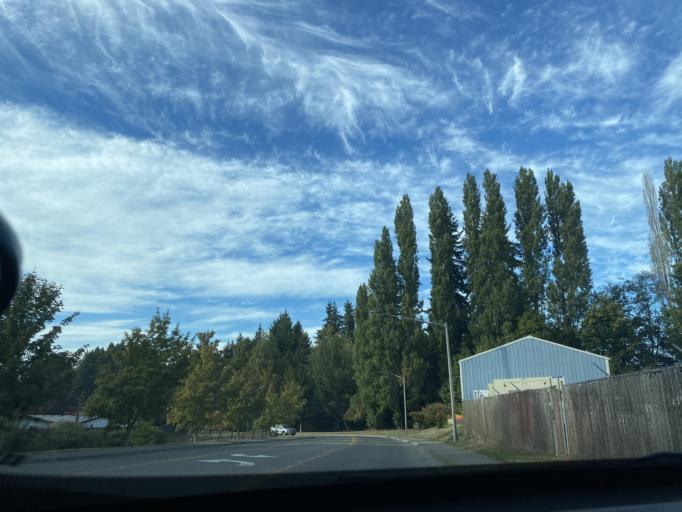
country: US
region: Washington
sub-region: Kitsap County
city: Poulsbo
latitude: 47.7364
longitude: -122.6402
